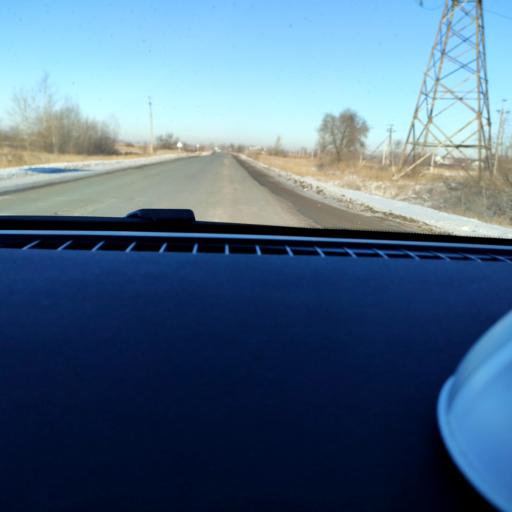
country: RU
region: Samara
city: Spiridonovka
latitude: 53.1118
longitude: 50.6387
